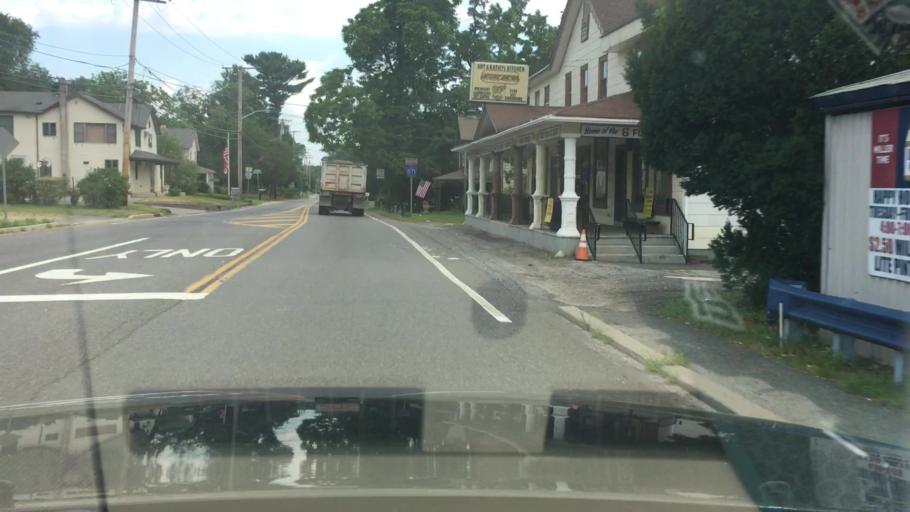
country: US
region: New Jersey
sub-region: Ocean County
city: Vista Center
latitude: 40.1049
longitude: -74.3867
